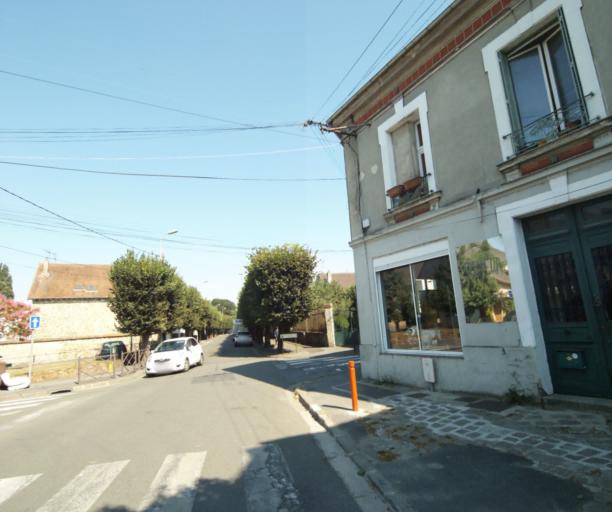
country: FR
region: Ile-de-France
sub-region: Departement de Seine-et-Marne
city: Pomponne
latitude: 48.8784
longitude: 2.6955
